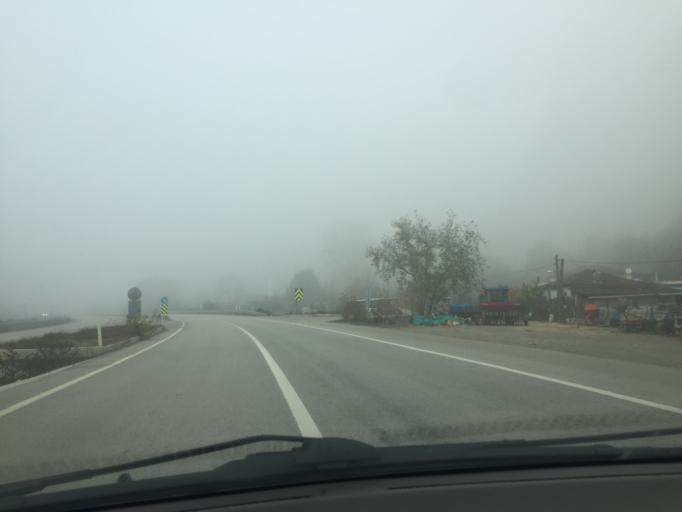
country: TR
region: Canakkale
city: Bakacak
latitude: 40.1028
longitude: 27.1718
